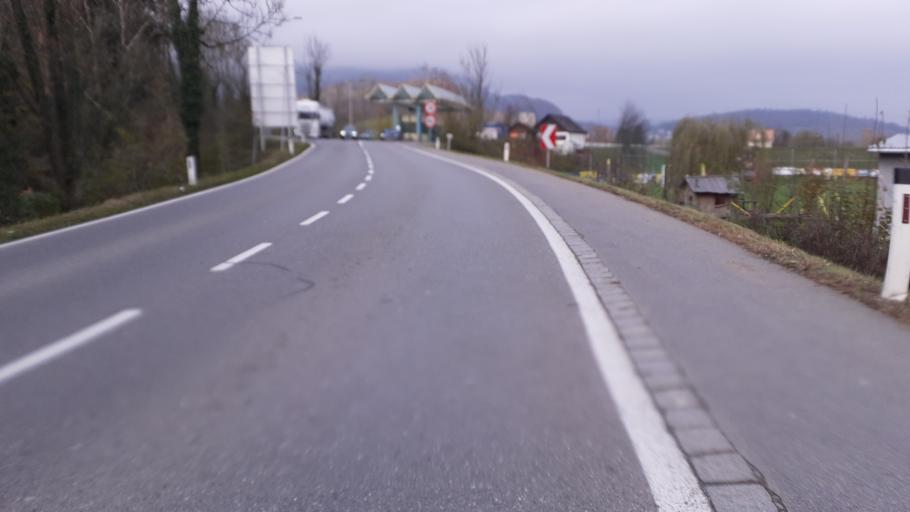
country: AT
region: Vorarlberg
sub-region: Politischer Bezirk Feldkirch
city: Meiningen
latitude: 47.3039
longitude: 9.5738
